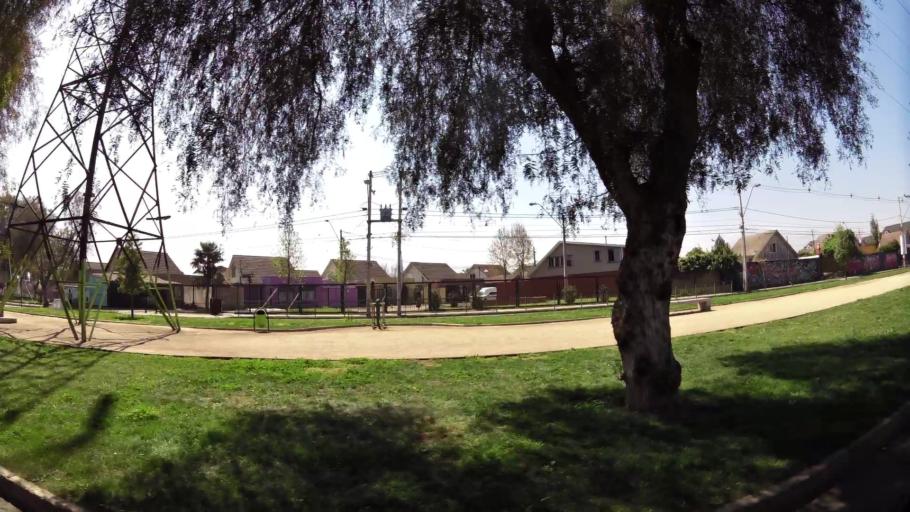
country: CL
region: Santiago Metropolitan
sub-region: Provincia de Santiago
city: Lo Prado
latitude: -33.3593
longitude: -70.7248
